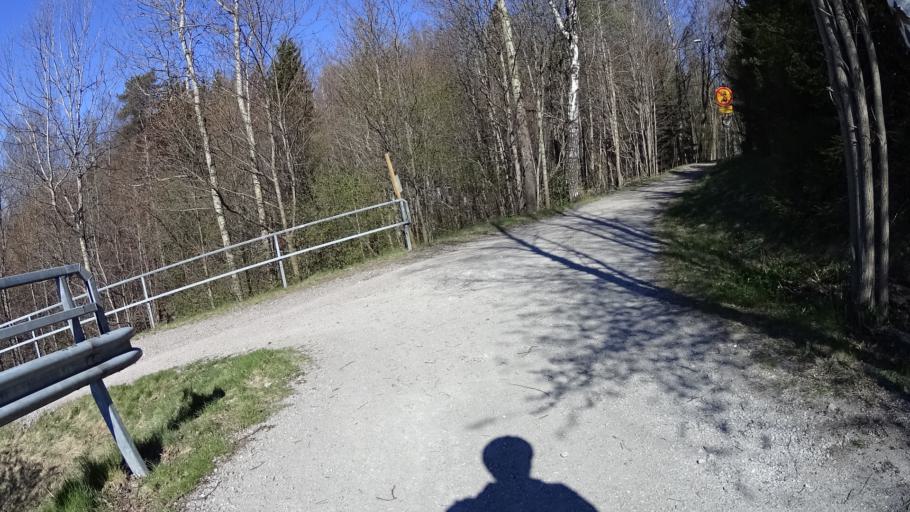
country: FI
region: Uusimaa
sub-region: Helsinki
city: Espoo
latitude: 60.2237
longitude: 24.6630
